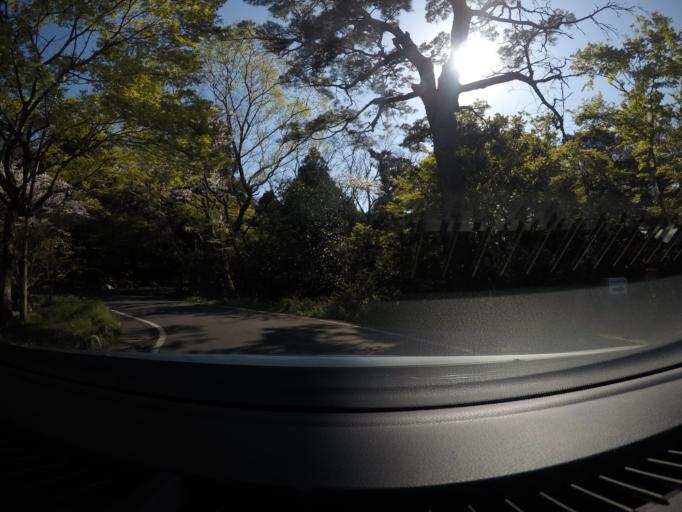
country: JP
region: Kochi
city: Kochi-shi
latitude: 33.5480
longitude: 133.5731
